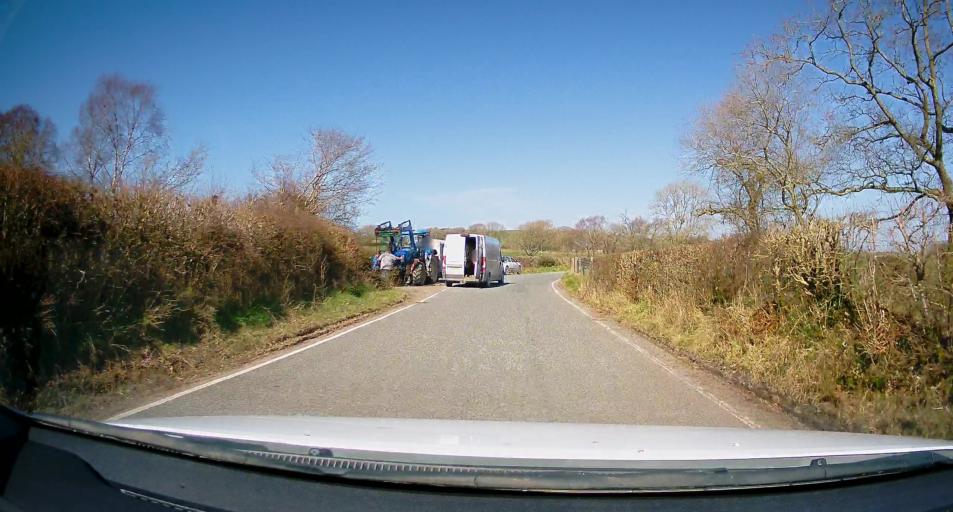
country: GB
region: Wales
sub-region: County of Ceredigion
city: Lledrod
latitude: 52.3115
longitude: -4.0622
